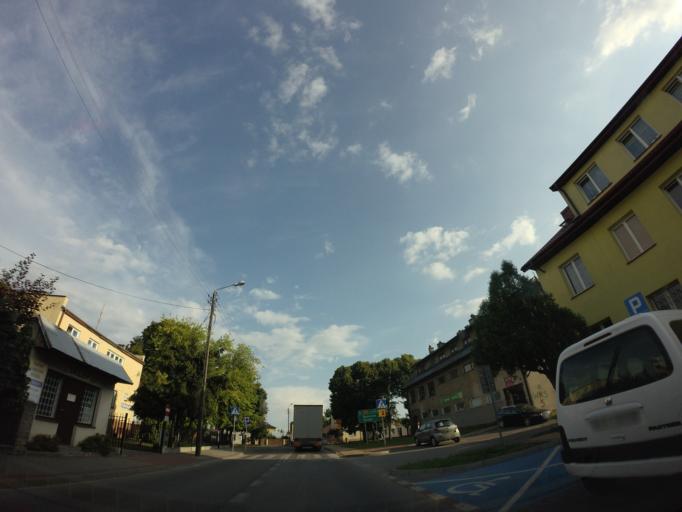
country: PL
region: Lublin Voivodeship
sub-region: Powiat lubartowski
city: Michow
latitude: 51.5239
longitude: 22.3143
